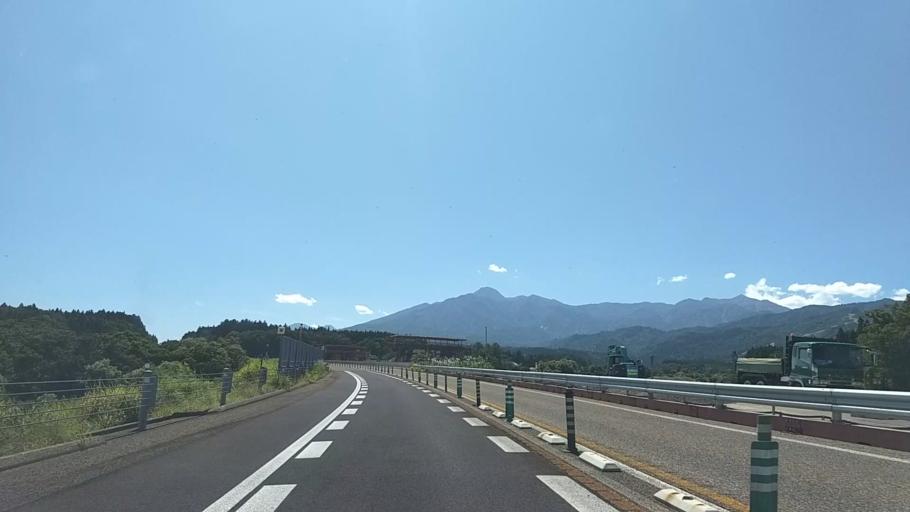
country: JP
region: Niigata
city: Arai
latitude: 37.0071
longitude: 138.2092
